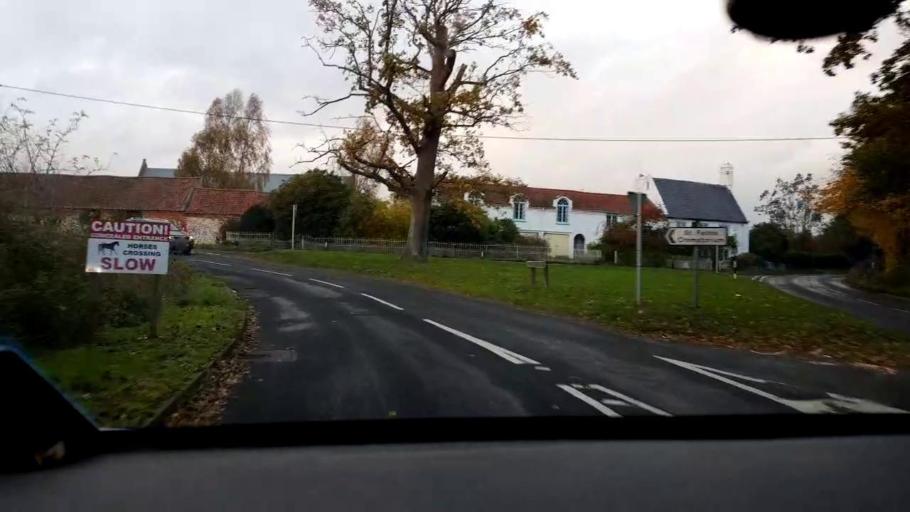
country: GB
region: England
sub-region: Norfolk
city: Spixworth
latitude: 52.6925
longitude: 1.3139
